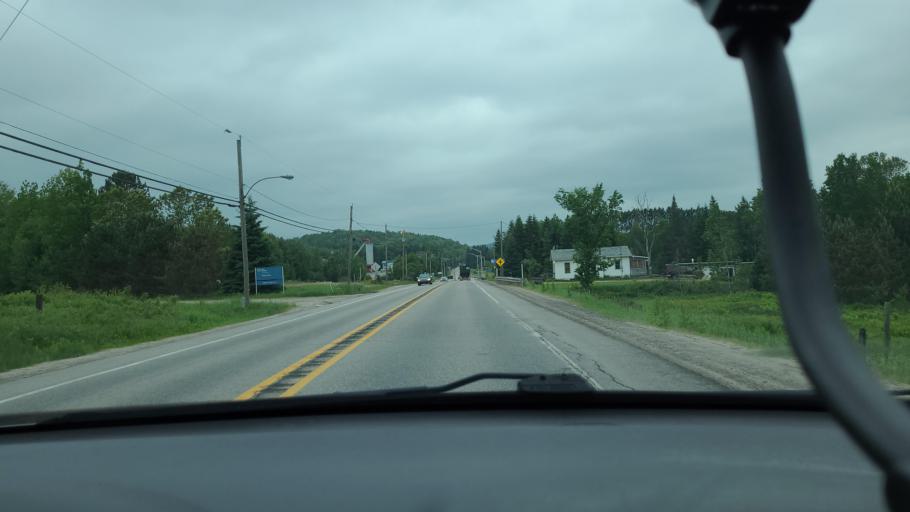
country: CA
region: Quebec
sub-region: Laurentides
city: Labelle
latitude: 46.2947
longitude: -74.7753
